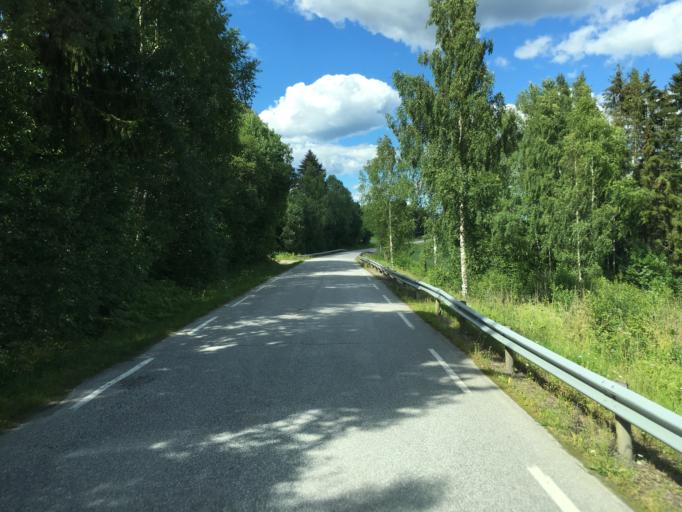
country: NO
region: Oppland
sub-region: Sondre Land
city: Hov
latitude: 60.5371
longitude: 10.2915
